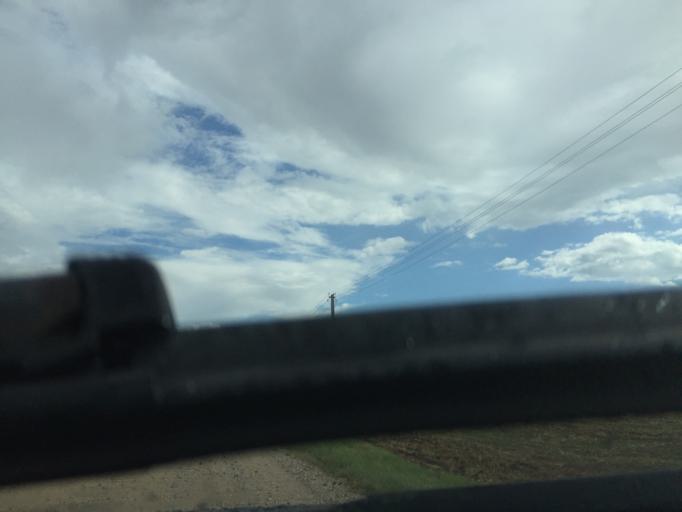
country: LT
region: Siauliu apskritis
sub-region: Joniskis
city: Joniskis
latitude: 56.3380
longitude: 23.5576
